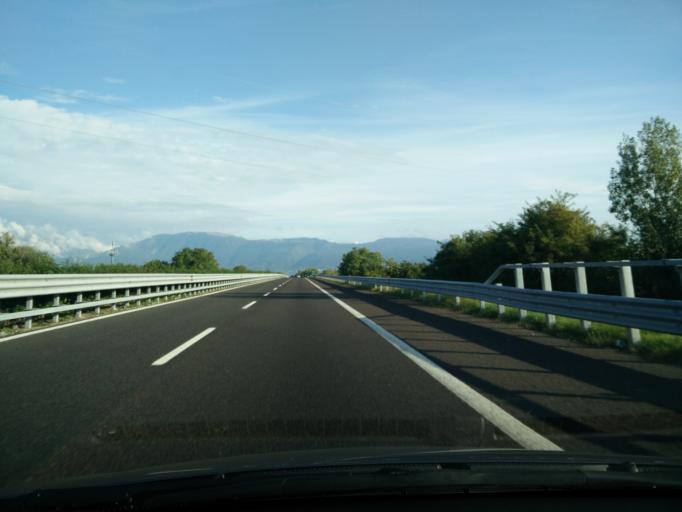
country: IT
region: Veneto
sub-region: Provincia di Treviso
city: San Martino
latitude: 45.8981
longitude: 12.3440
